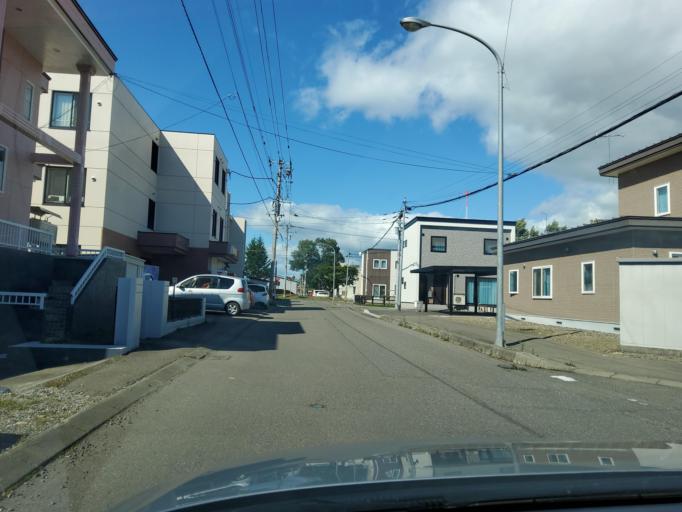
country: JP
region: Hokkaido
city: Obihiro
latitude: 42.9523
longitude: 143.1950
